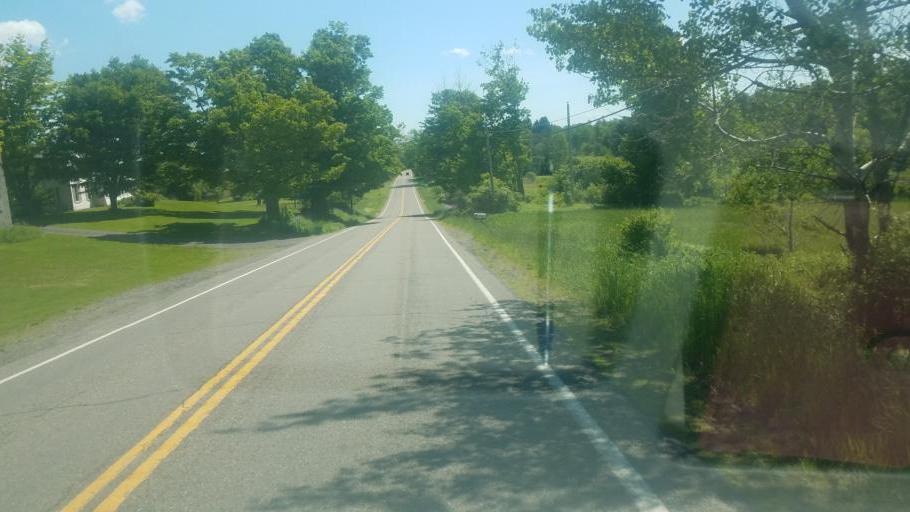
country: US
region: Pennsylvania
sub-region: Tioga County
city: Wellsboro
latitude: 41.7346
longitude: -77.3622
